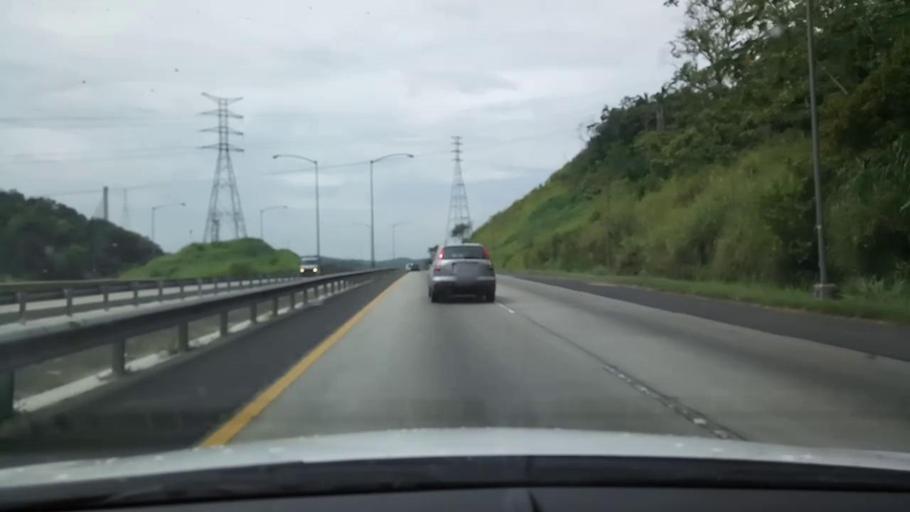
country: PA
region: Panama
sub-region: Distrito de Panama
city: Paraiso
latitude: 9.0369
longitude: -79.6272
